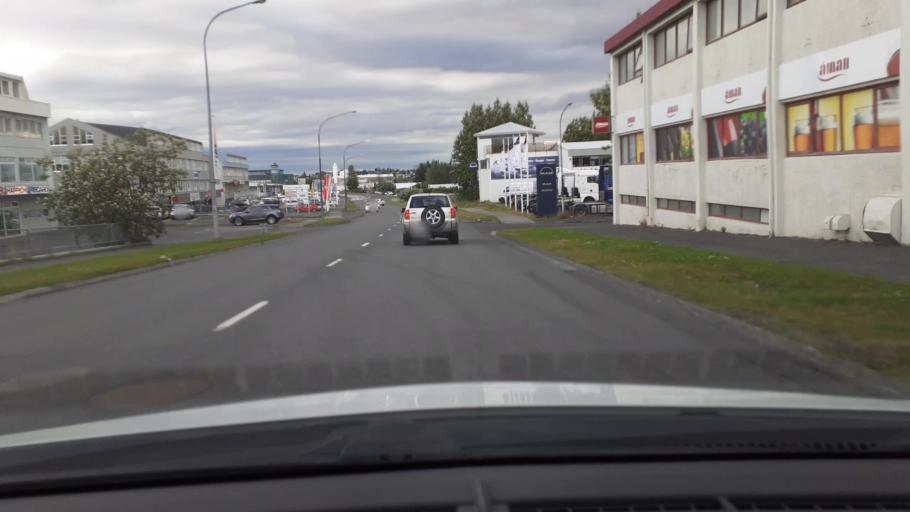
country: IS
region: Capital Region
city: Reykjavik
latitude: 64.1257
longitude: -21.8171
